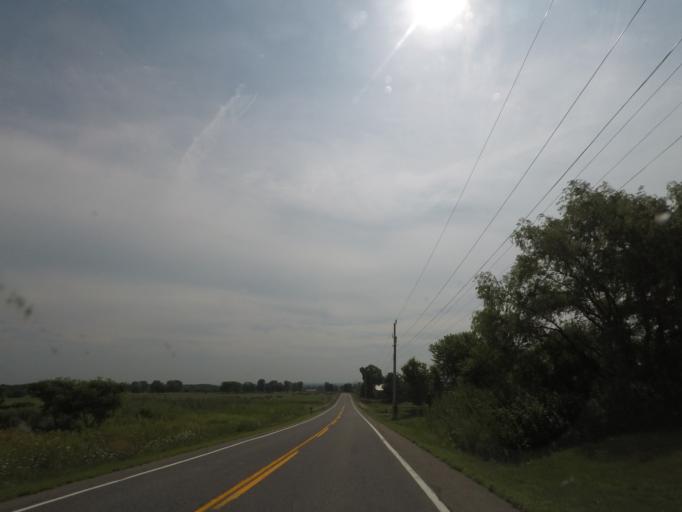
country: US
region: New York
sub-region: Saratoga County
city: Mechanicville
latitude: 42.8891
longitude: -73.7156
